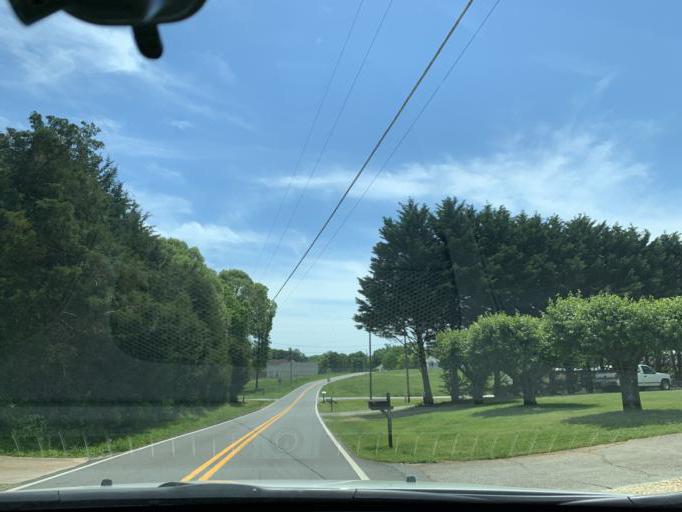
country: US
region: Georgia
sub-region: Hall County
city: Flowery Branch
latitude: 34.2796
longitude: -84.0225
